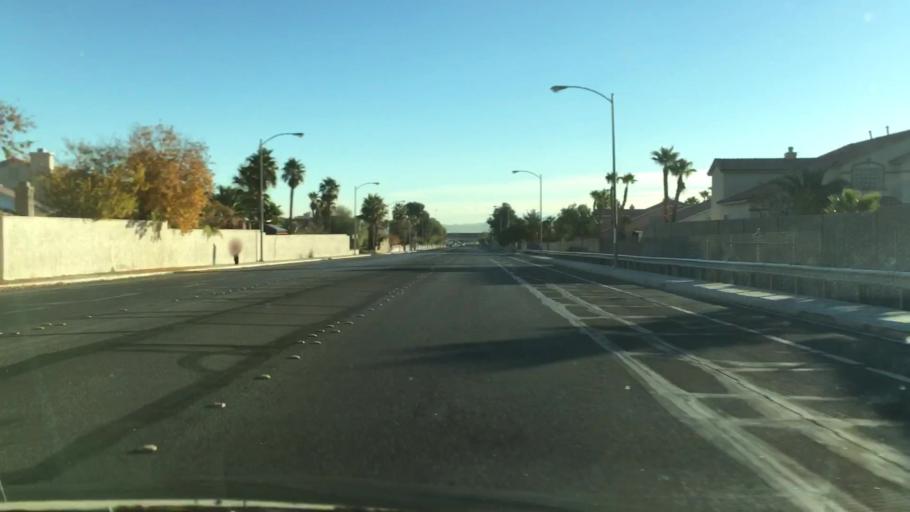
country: US
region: Nevada
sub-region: Clark County
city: Paradise
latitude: 36.0497
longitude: -115.1472
